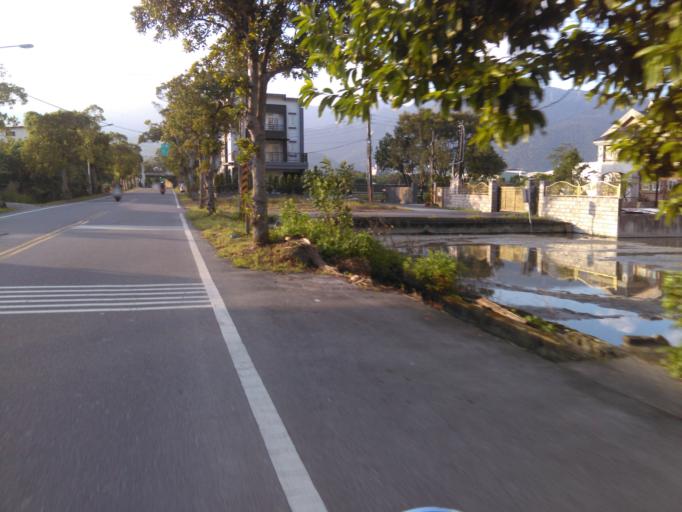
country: TW
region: Taiwan
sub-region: Yilan
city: Yilan
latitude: 24.8077
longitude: 121.7702
